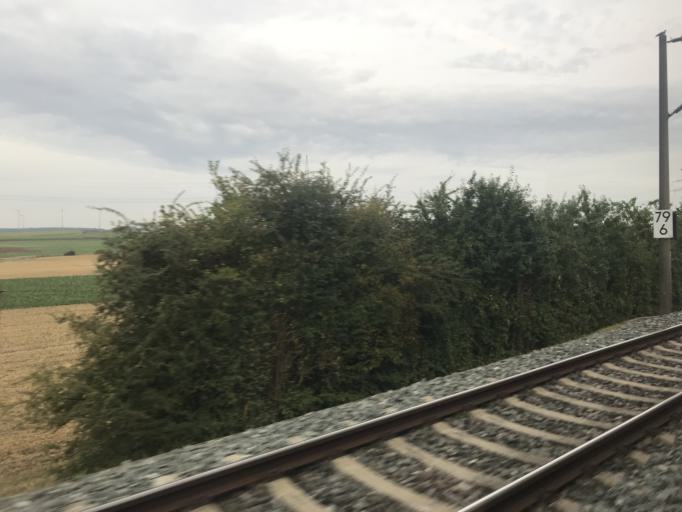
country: DE
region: Bavaria
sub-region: Regierungsbezirk Unterfranken
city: Oberpleichfeld
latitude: 49.8818
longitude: 10.0921
